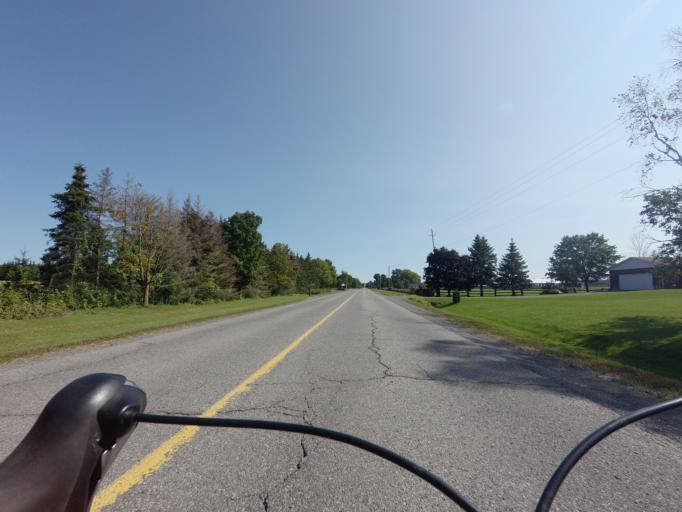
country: CA
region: Ontario
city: Carleton Place
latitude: 45.3508
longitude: -76.1131
